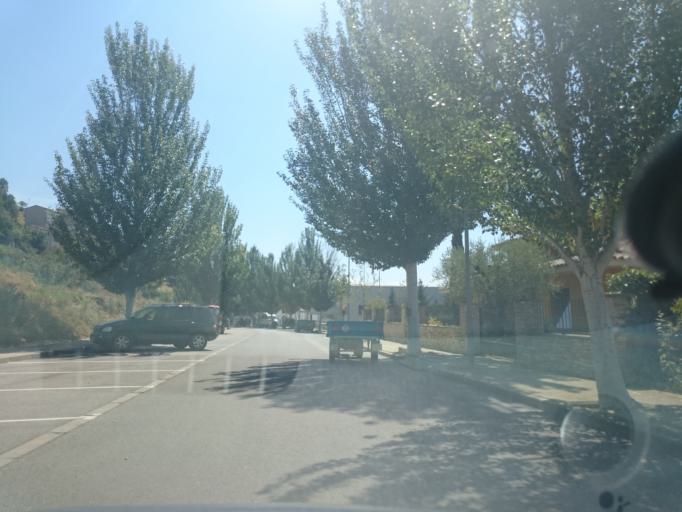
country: ES
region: Catalonia
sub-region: Provincia de Barcelona
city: Sant Pere de Riudebitlles
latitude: 41.4639
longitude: 1.6578
